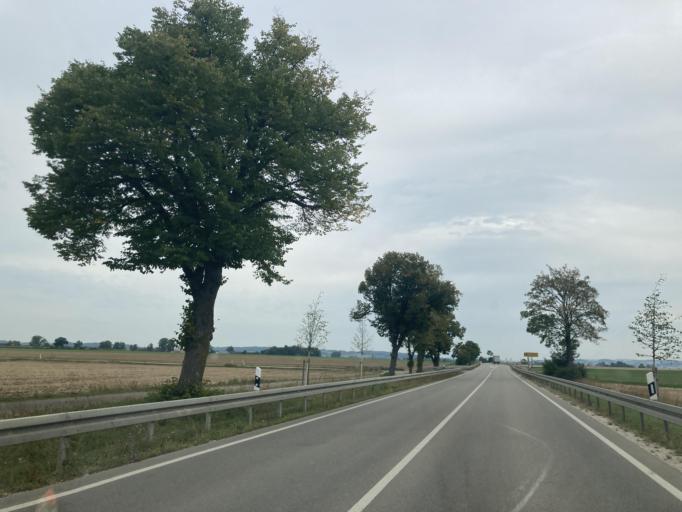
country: DE
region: Bavaria
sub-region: Swabia
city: Munningen
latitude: 48.9202
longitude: 10.5734
